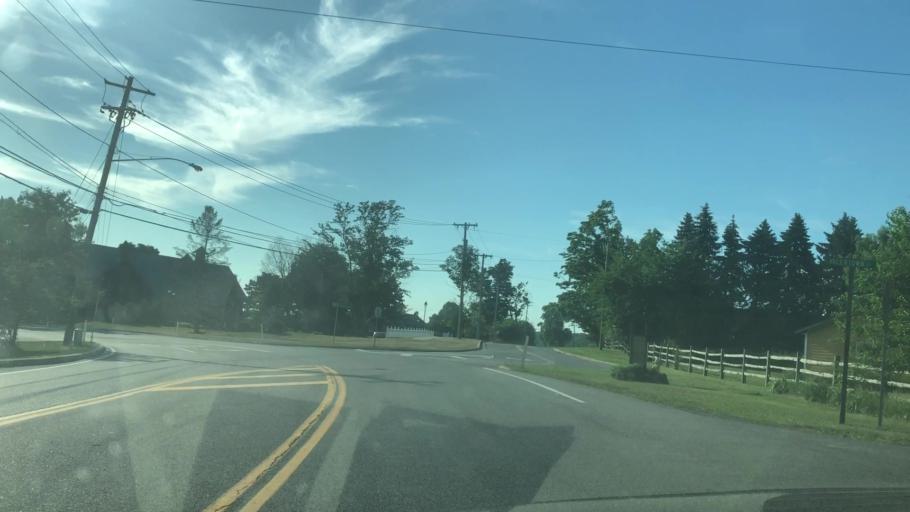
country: US
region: New York
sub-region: Ontario County
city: Victor
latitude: 43.0257
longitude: -77.4365
